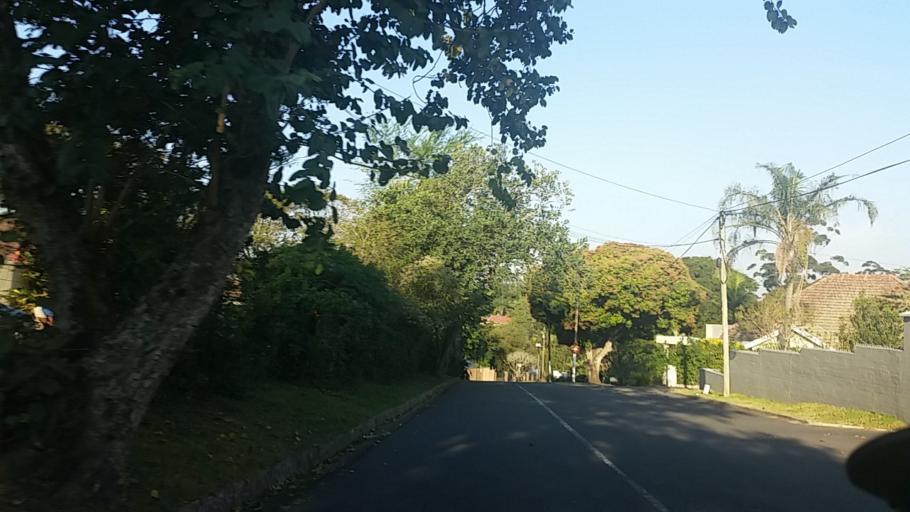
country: ZA
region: KwaZulu-Natal
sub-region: eThekwini Metropolitan Municipality
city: Berea
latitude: -29.8391
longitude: 30.9137
